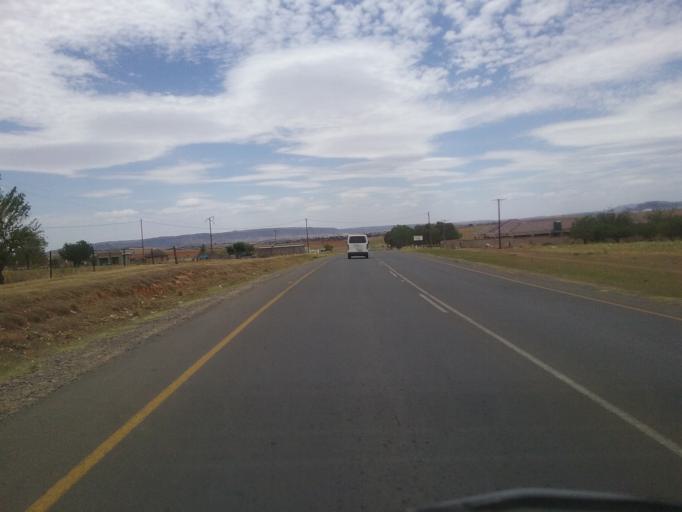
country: LS
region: Maseru
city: Maseru
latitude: -29.4813
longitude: 27.5273
